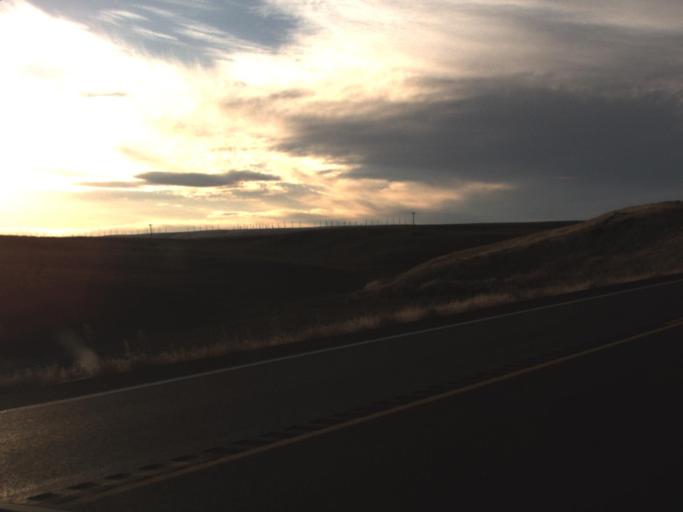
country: US
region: Washington
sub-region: Walla Walla County
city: Garrett
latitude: 46.0550
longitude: -118.7177
